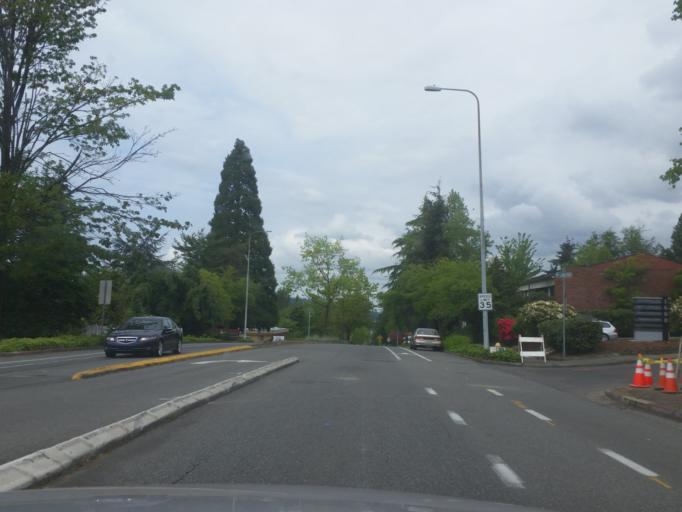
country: US
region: Washington
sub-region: King County
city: Kirkland
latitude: 47.6880
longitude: -122.2098
